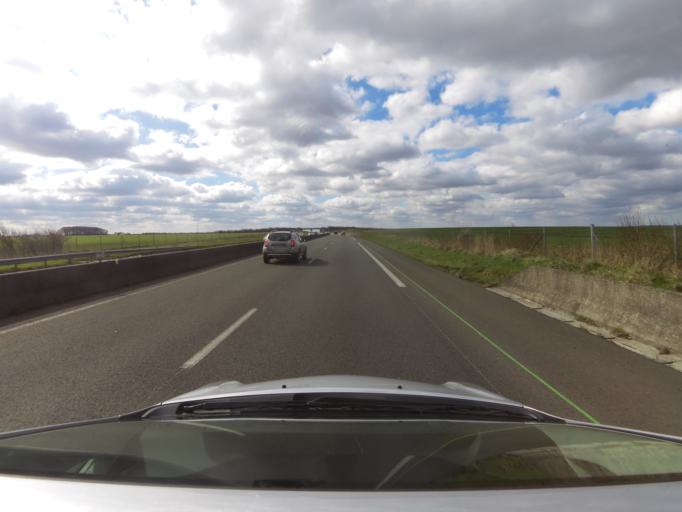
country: FR
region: Picardie
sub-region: Departement de la Somme
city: Sailly-Flibeaucourt
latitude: 50.1849
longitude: 1.7544
